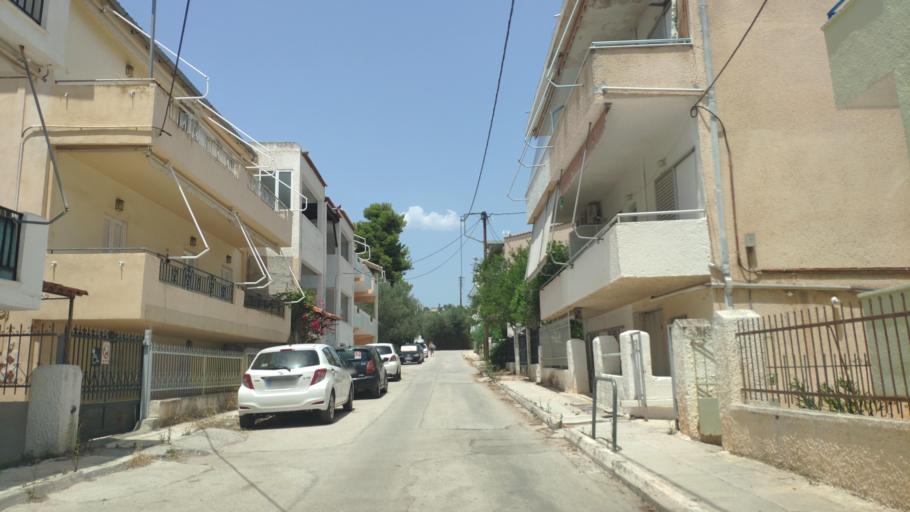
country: GR
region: Peloponnese
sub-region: Nomos Argolidos
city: Porto Cheli
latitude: 37.3286
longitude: 23.1483
